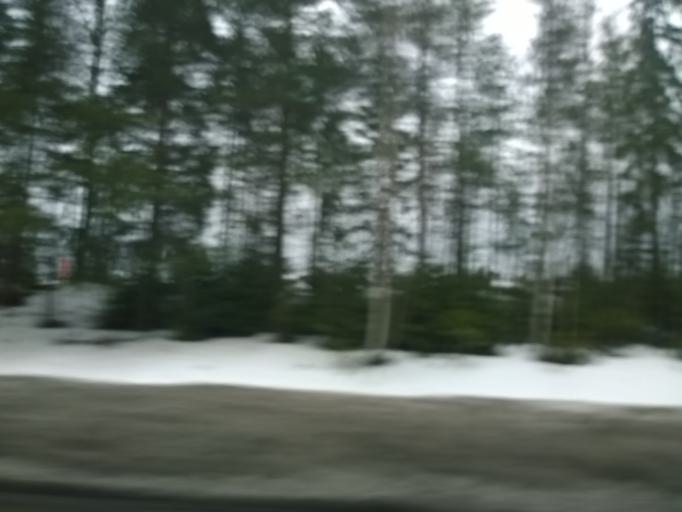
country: FI
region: Pirkanmaa
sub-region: Tampere
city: Tampere
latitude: 61.4185
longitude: 23.7576
